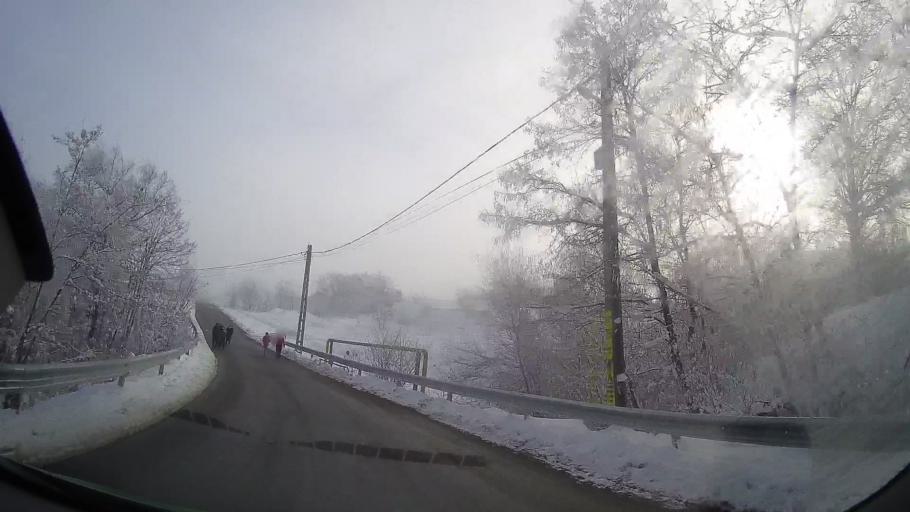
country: RO
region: Iasi
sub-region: Comuna Valea Seaca
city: Topile
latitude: 47.2468
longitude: 26.6608
